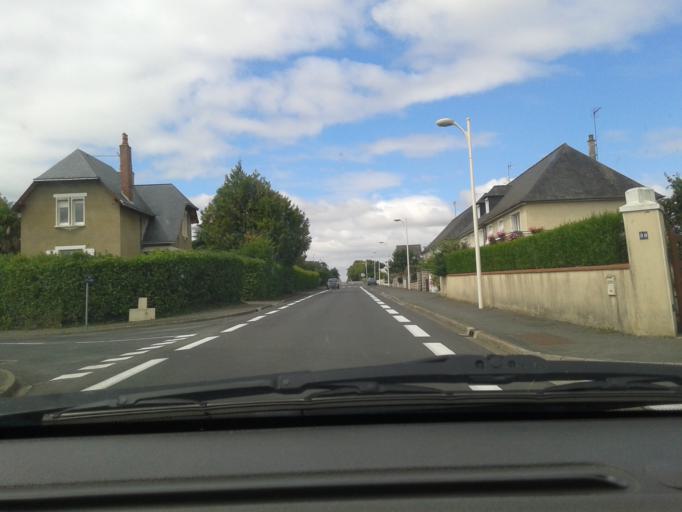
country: FR
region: Pays de la Loire
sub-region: Departement de Maine-et-Loire
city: Grez-Neuville
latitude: 47.6237
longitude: -0.7190
